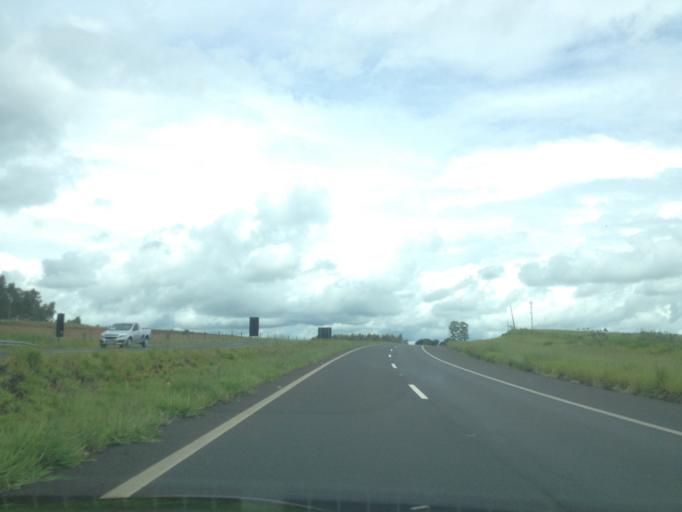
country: BR
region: Sao Paulo
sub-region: Duartina
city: Duartina
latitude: -22.3250
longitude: -49.3950
